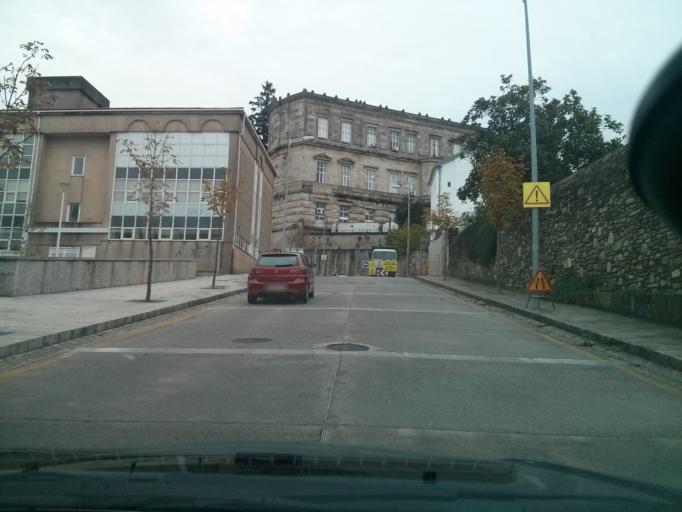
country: ES
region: Galicia
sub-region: Provincia da Coruna
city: Santiago de Compostela
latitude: 42.8825
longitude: -8.5478
